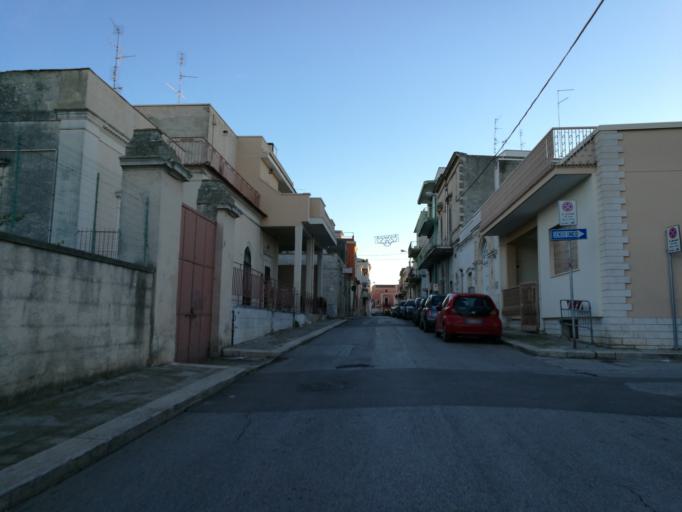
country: IT
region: Apulia
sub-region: Provincia di Bari
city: Adelfia
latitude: 41.0063
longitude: 16.8778
